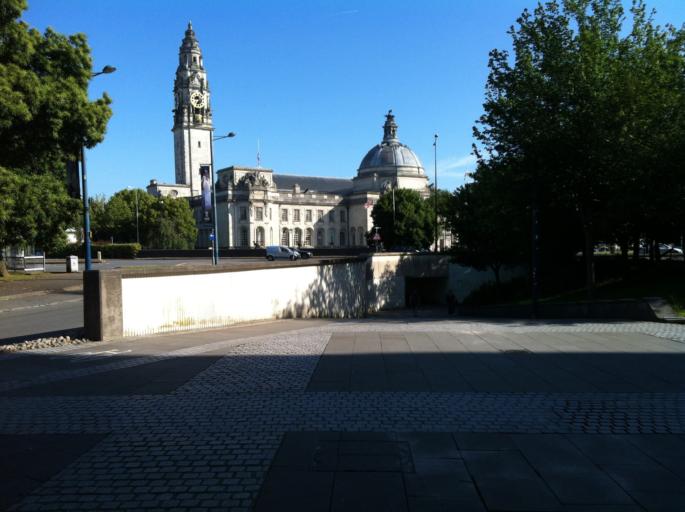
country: GB
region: Wales
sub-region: Cardiff
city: Cardiff
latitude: 51.4836
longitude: -3.1783
